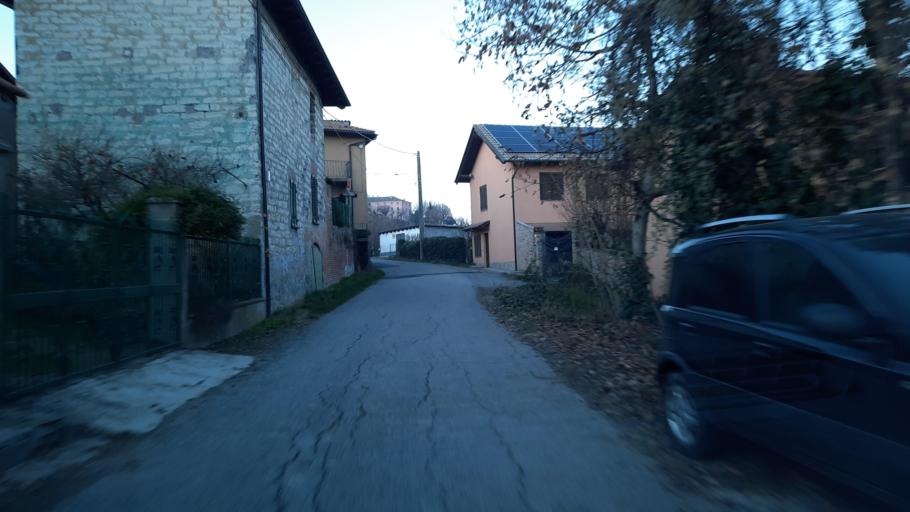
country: IT
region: Piedmont
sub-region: Provincia di Alessandria
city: Camino
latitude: 45.1568
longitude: 8.2840
